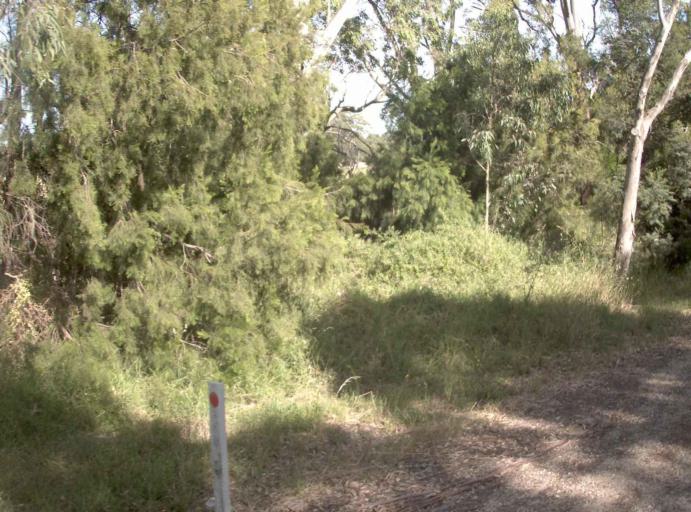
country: AU
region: Victoria
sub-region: East Gippsland
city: Lakes Entrance
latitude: -37.7969
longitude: 147.8323
